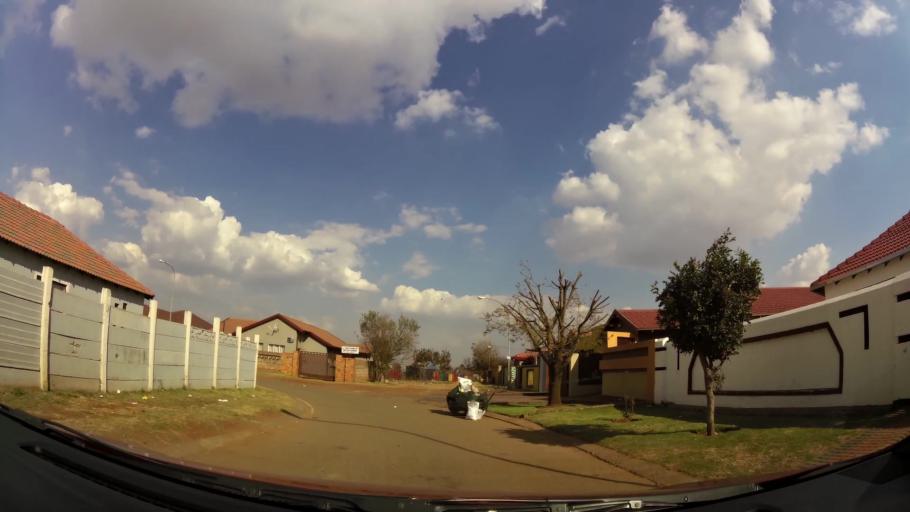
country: ZA
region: Gauteng
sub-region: City of Johannesburg Metropolitan Municipality
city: Soweto
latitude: -26.2179
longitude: 27.8608
